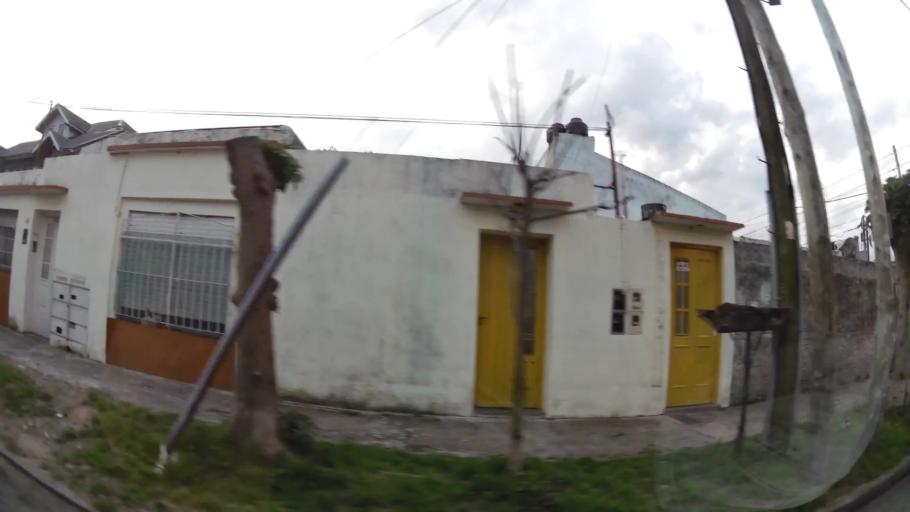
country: AR
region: Buenos Aires
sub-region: Partido de Quilmes
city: Quilmes
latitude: -34.7407
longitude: -58.2440
